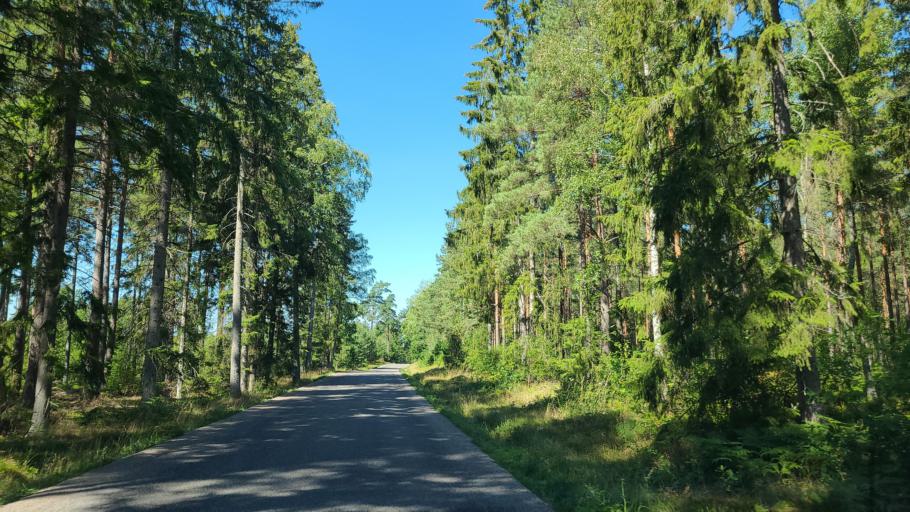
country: SE
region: Kalmar
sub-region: Kalmar Kommun
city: Ljungbyholm
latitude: 56.5715
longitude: 16.0305
